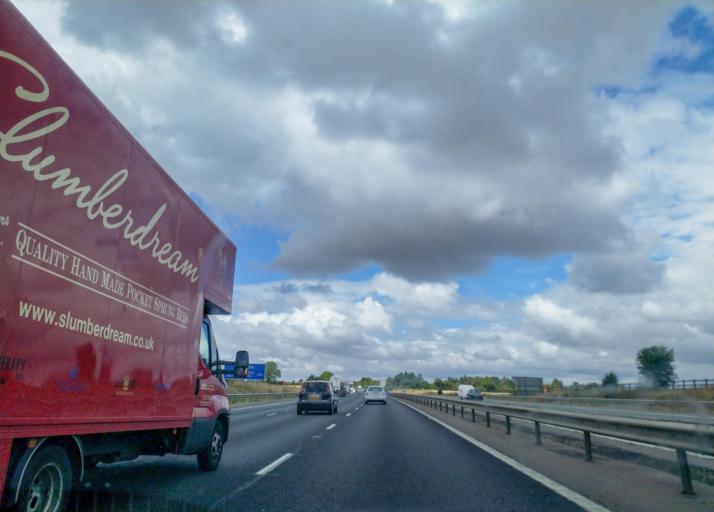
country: GB
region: England
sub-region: Oxfordshire
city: Somerton
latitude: 51.9588
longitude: -1.2162
